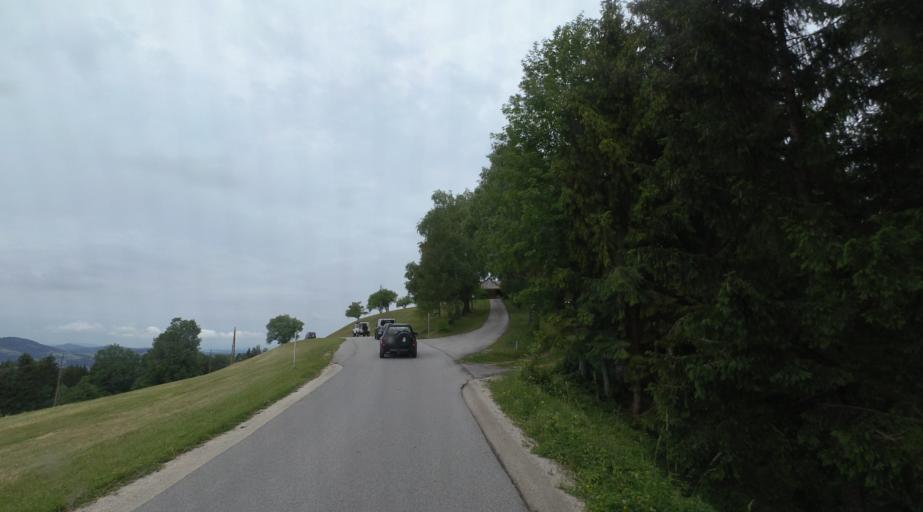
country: AT
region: Upper Austria
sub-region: Politischer Bezirk Kirchdorf an der Krems
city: Micheldorf in Oberoesterreich
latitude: 47.9361
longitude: 14.1678
